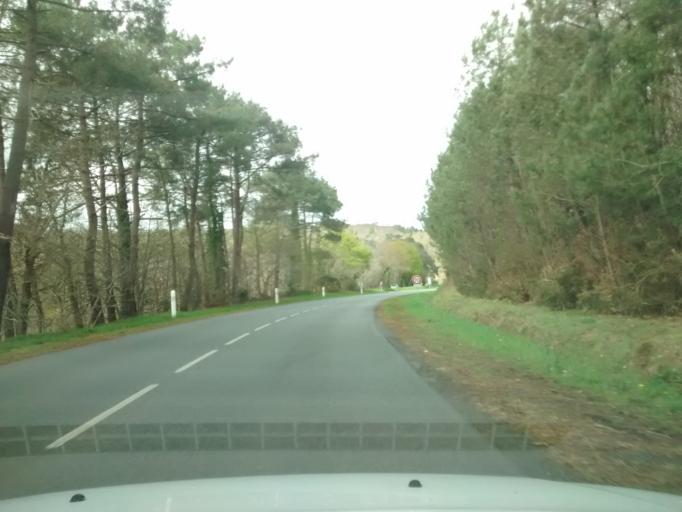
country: FR
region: Brittany
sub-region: Departement du Morbihan
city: Guidel-Plage
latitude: 47.7937
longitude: -3.5243
